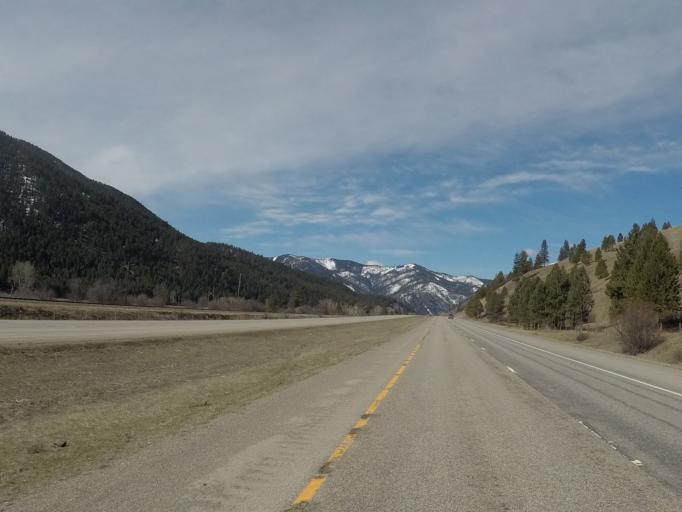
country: US
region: Montana
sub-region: Missoula County
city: Clinton
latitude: 46.7255
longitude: -113.6135
